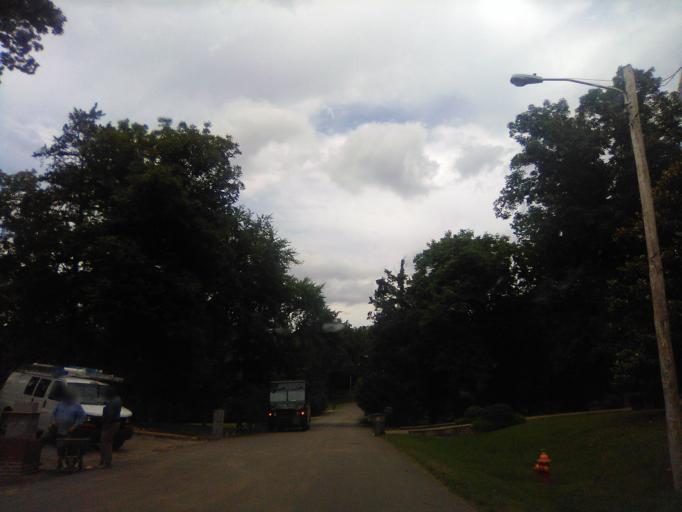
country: US
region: Tennessee
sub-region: Davidson County
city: Belle Meade
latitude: 36.1267
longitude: -86.8793
